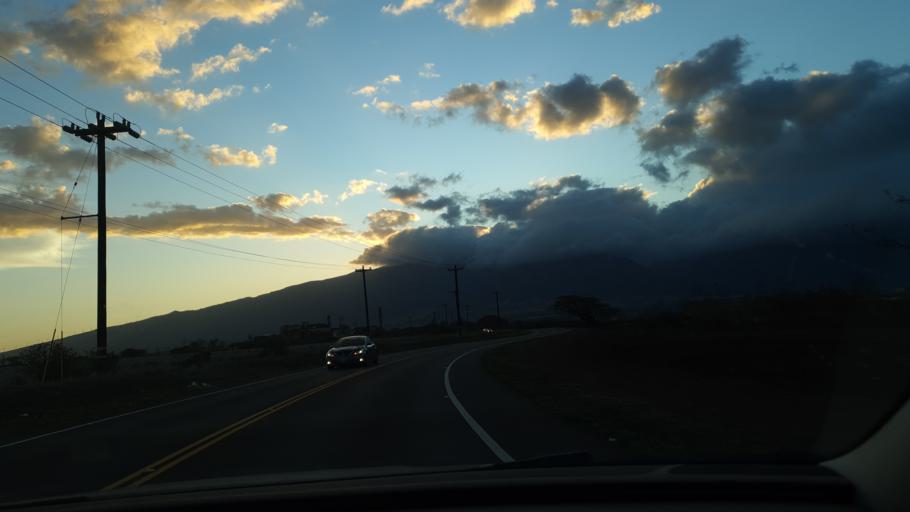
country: US
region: Hawaii
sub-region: Maui County
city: Kahului
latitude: 20.8712
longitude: -156.4439
